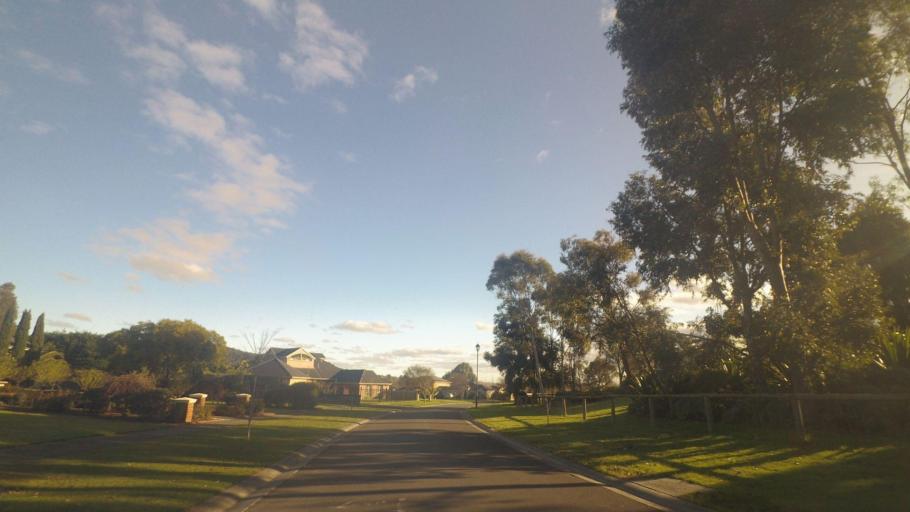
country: AU
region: Victoria
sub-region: Yarra Ranges
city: Lysterfield
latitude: -37.9153
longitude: 145.2917
